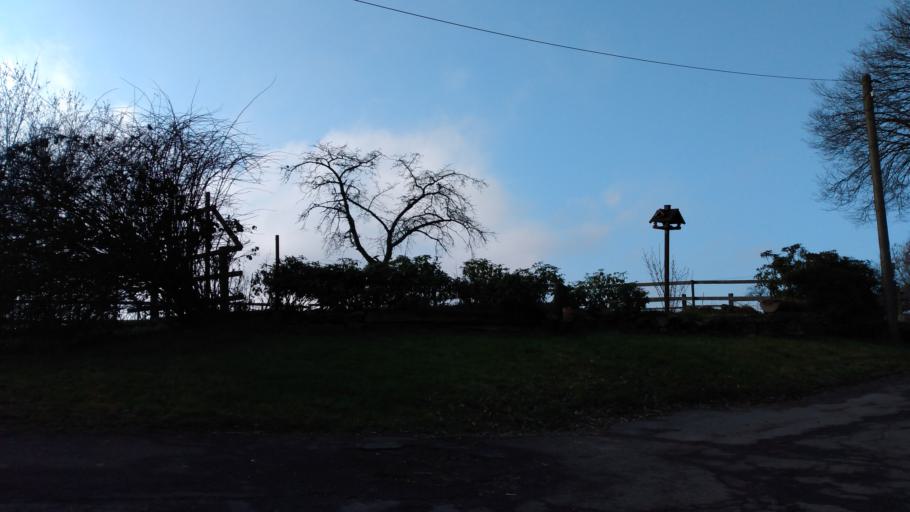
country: DE
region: Rheinland-Pfalz
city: Hirz-Maulsbach
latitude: 50.6807
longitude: 7.4610
